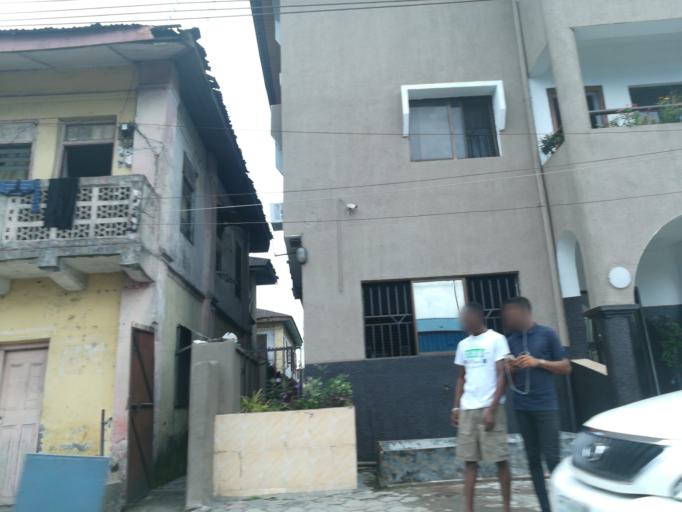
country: NG
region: Rivers
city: Port Harcourt
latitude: 4.7603
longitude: 7.0207
